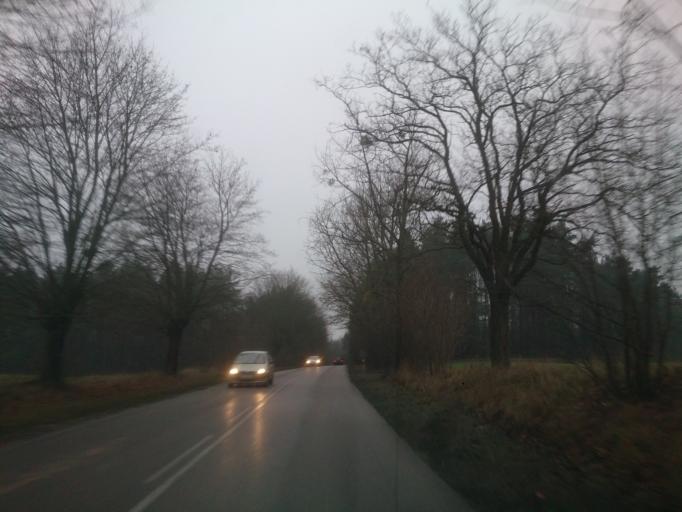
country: PL
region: Pomeranian Voivodeship
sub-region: Powiat koscierski
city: Koscierzyna
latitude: 54.0463
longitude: 18.0549
